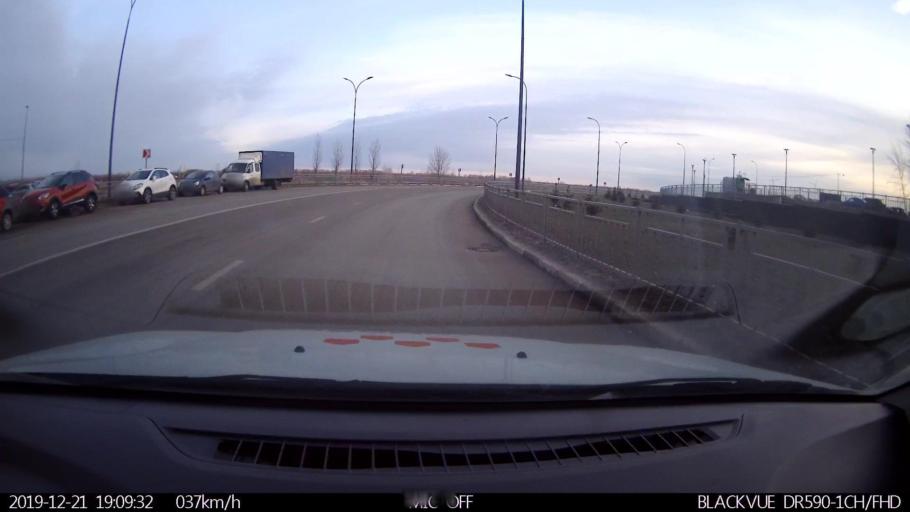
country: RU
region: Nizjnij Novgorod
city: Nizhniy Novgorod
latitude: 56.3464
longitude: 43.9375
